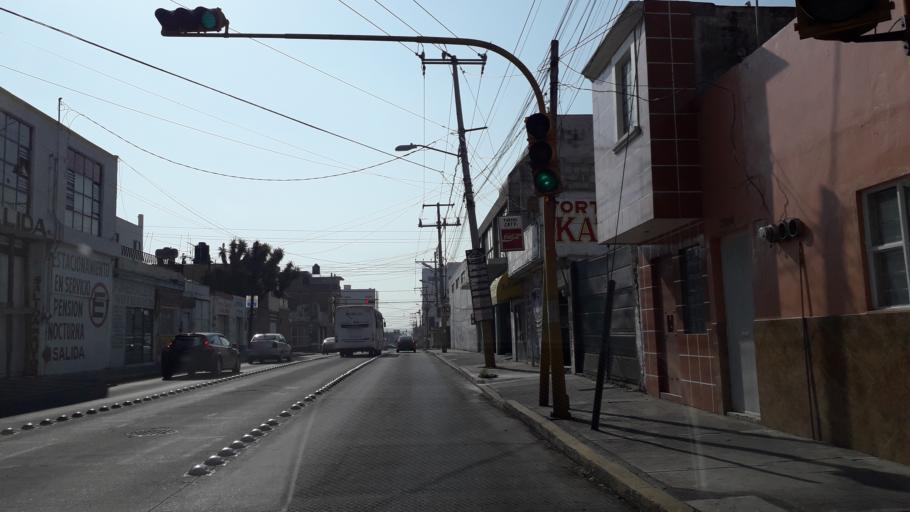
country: MX
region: Puebla
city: Puebla
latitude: 19.0578
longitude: -98.2151
